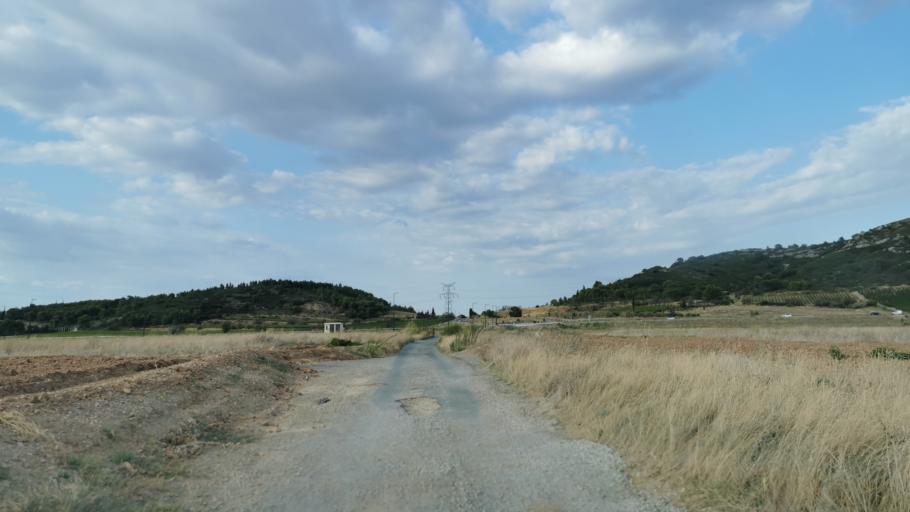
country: FR
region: Languedoc-Roussillon
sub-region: Departement de l'Aude
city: Nevian
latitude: 43.1951
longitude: 2.8962
